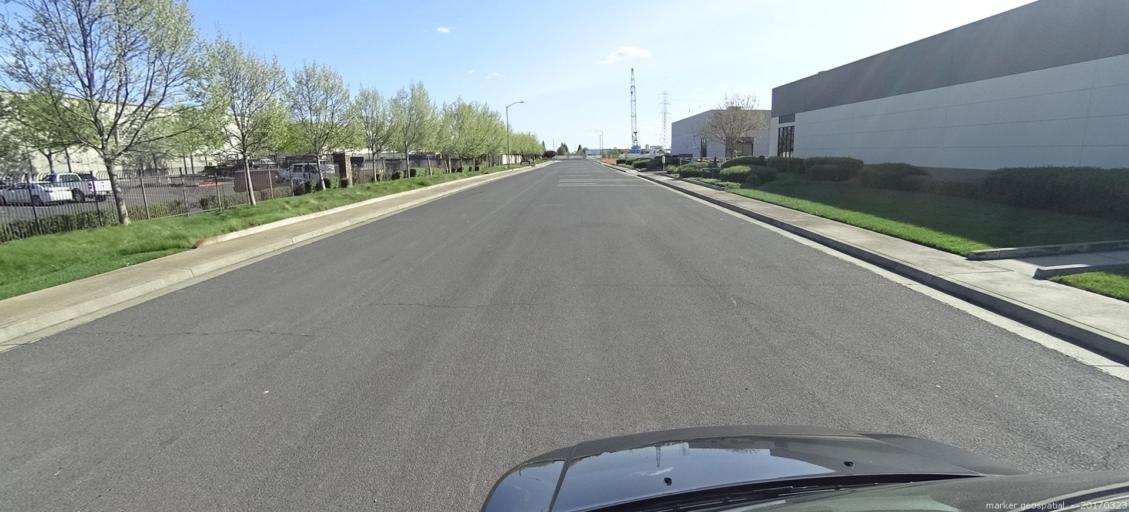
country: US
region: California
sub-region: Sacramento County
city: Florin
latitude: 38.5214
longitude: -121.3849
